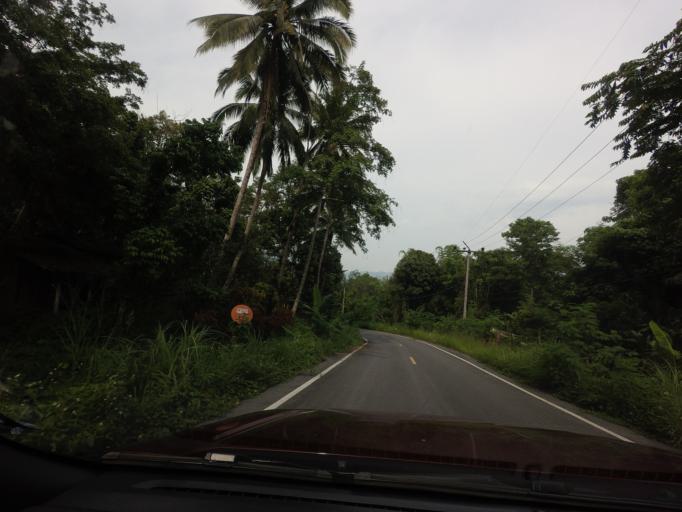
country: TH
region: Yala
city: Than To
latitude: 6.0706
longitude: 101.3498
